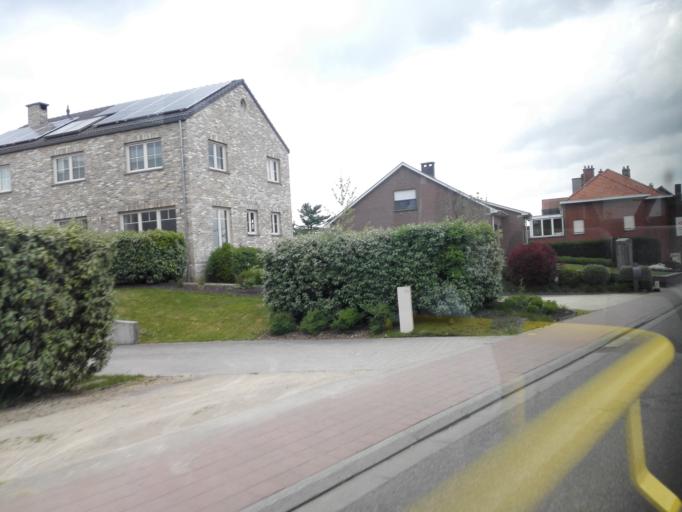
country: BE
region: Flanders
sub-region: Provincie Vlaams-Brabant
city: Tervuren
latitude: 50.8142
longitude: 4.5411
